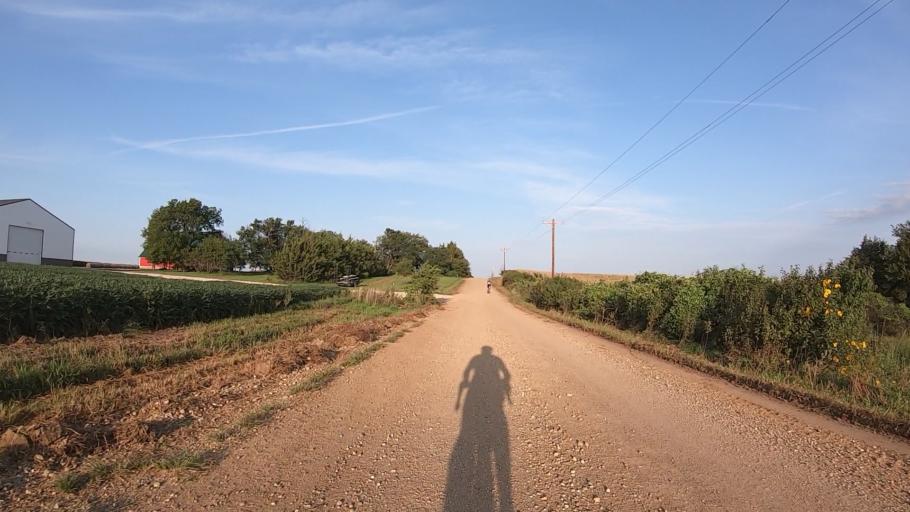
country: US
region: Kansas
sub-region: Marshall County
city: Marysville
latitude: 39.7694
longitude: -96.7465
